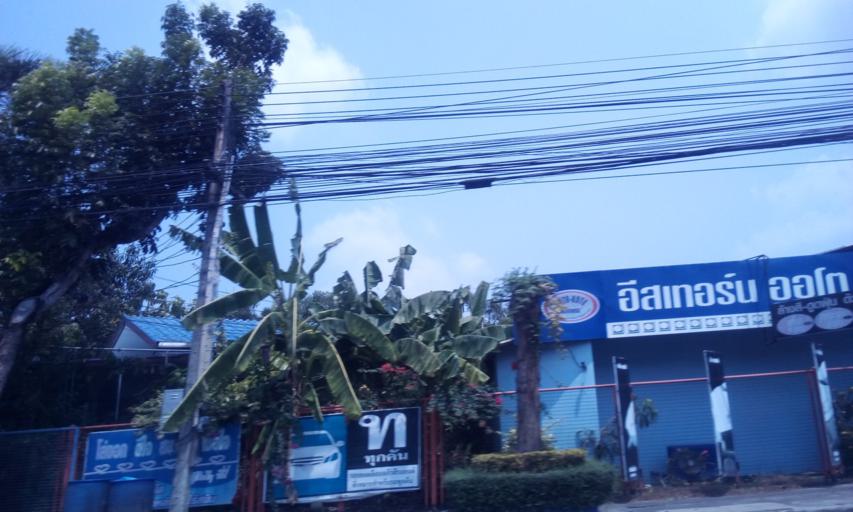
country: TH
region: Chachoengsao
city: Chachoengsao
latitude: 13.6830
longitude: 101.0800
